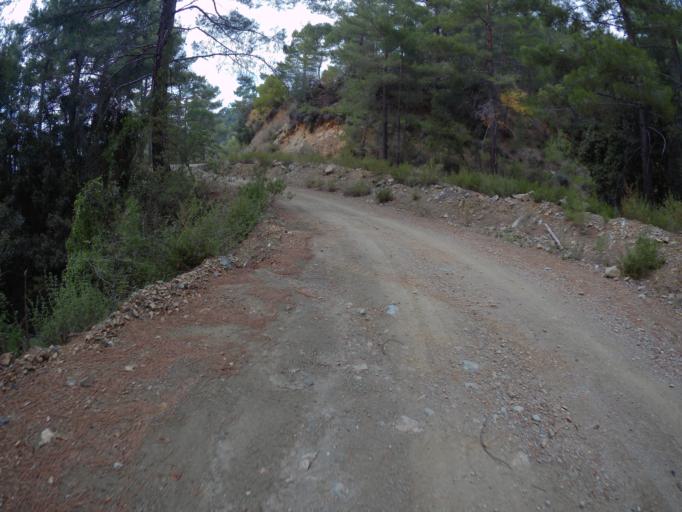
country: CY
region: Limassol
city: Pelendri
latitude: 34.8920
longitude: 32.8864
